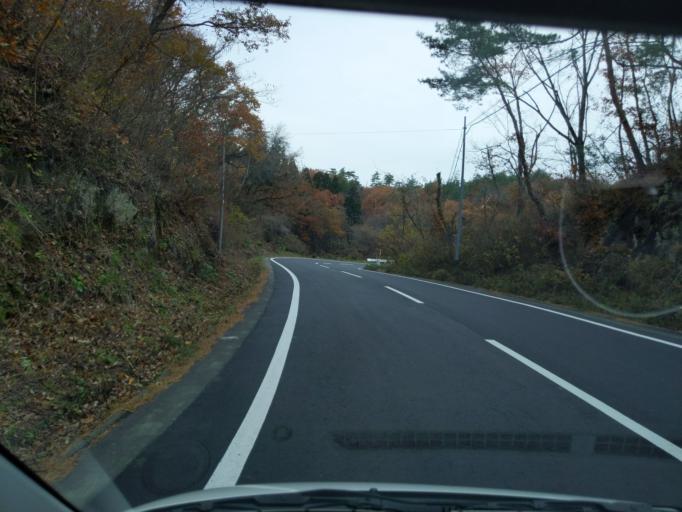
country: JP
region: Iwate
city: Kitakami
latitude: 39.2404
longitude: 141.2175
